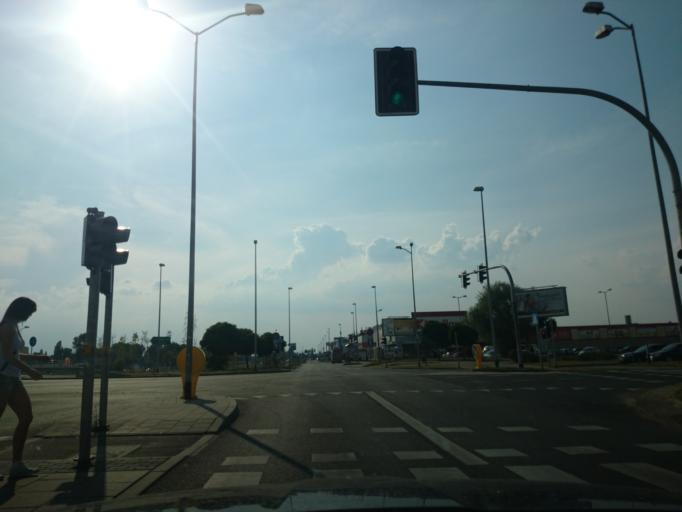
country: PL
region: West Pomeranian Voivodeship
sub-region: Szczecin
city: Szczecin
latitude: 53.3839
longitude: 14.6605
